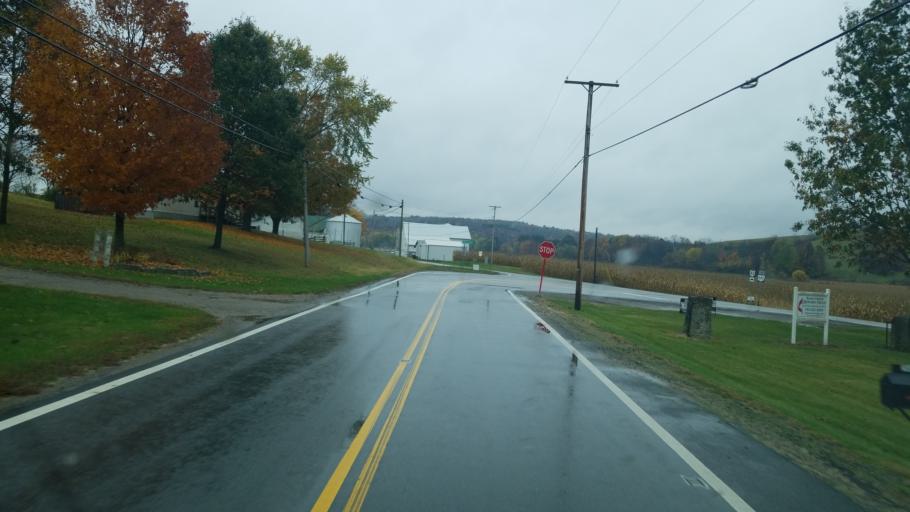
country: US
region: Ohio
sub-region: Coshocton County
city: Coshocton
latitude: 40.3316
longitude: -81.8640
